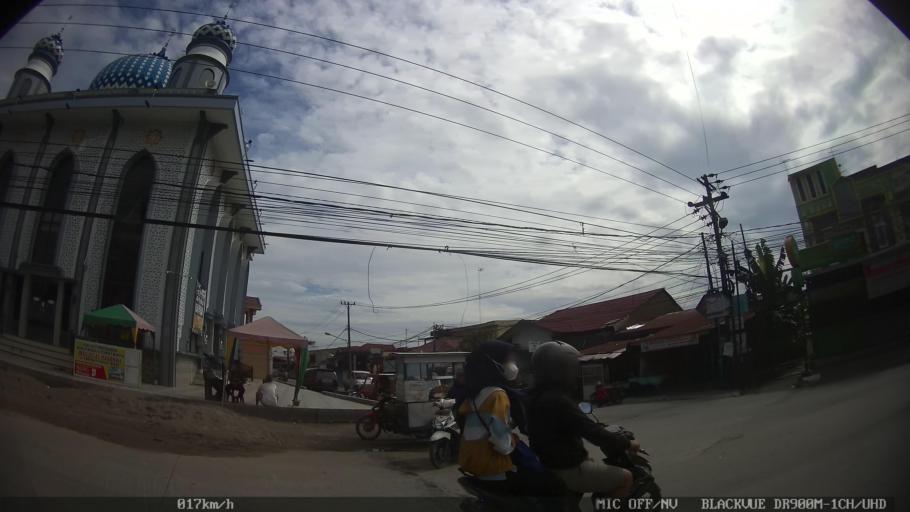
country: ID
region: North Sumatra
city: Sunggal
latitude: 3.6090
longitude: 98.6122
